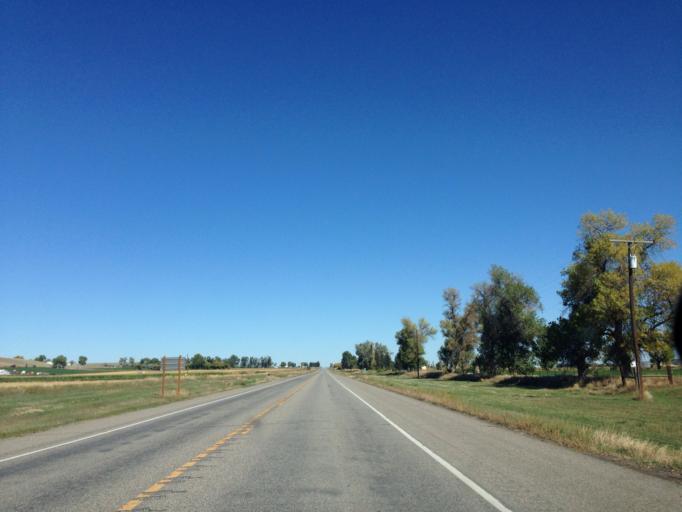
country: US
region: Montana
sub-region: Yellowstone County
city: Laurel
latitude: 45.4659
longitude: -108.8630
